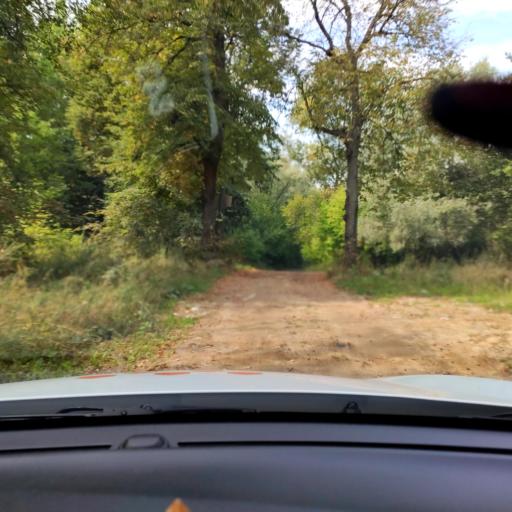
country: RU
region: Tatarstan
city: Staroye Arakchino
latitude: 55.8024
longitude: 48.9823
